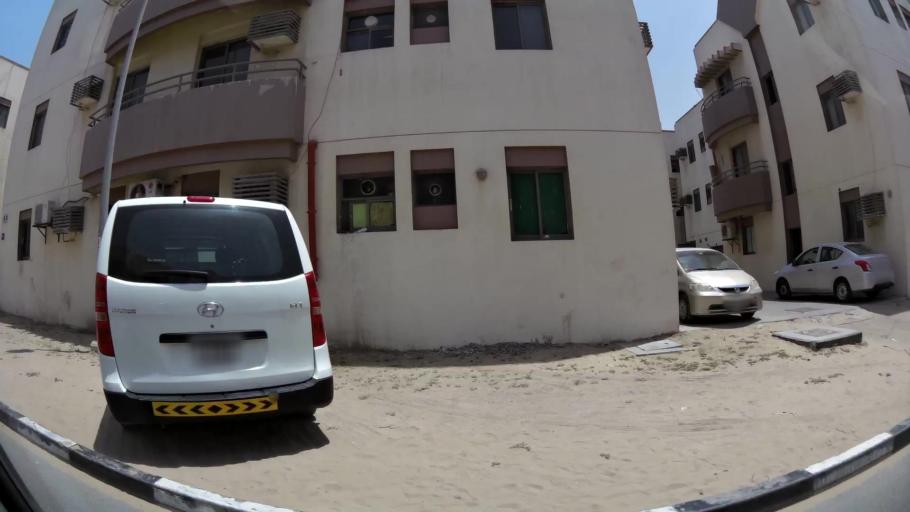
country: AE
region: Ash Shariqah
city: Sharjah
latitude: 25.2822
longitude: 55.4099
